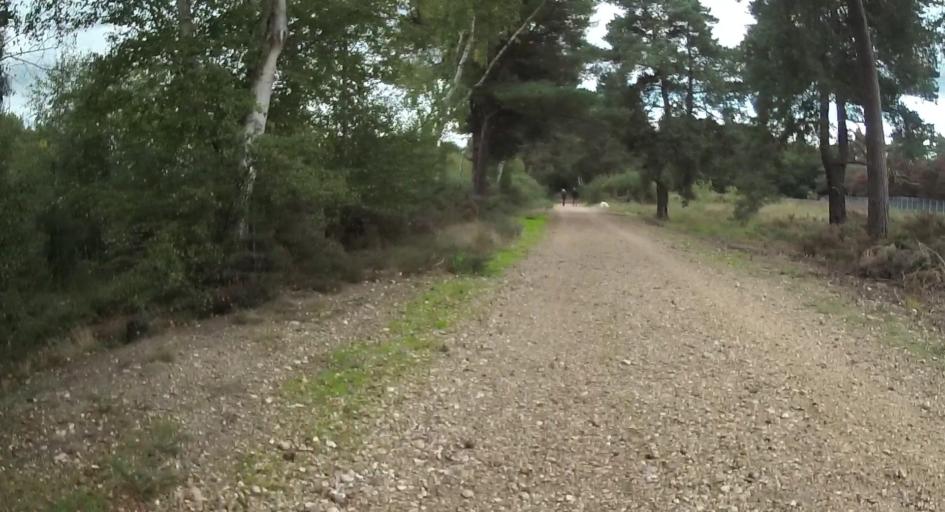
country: GB
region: England
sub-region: Surrey
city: Windlesham
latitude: 51.3404
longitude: -0.6636
